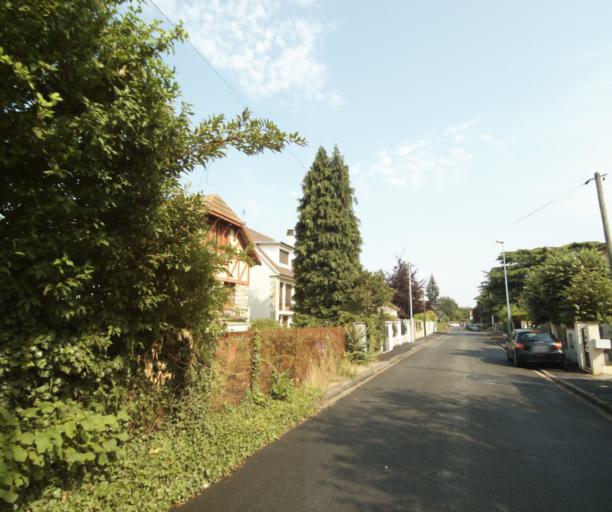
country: FR
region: Ile-de-France
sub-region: Departement des Yvelines
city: Maurecourt
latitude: 48.9981
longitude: 2.0758
